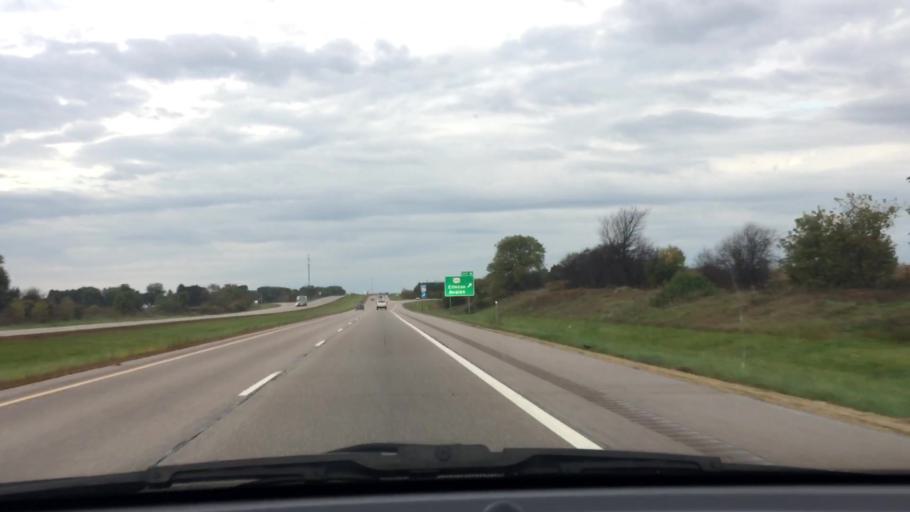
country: US
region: Wisconsin
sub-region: Rock County
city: Clinton
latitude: 42.5728
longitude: -88.8555
